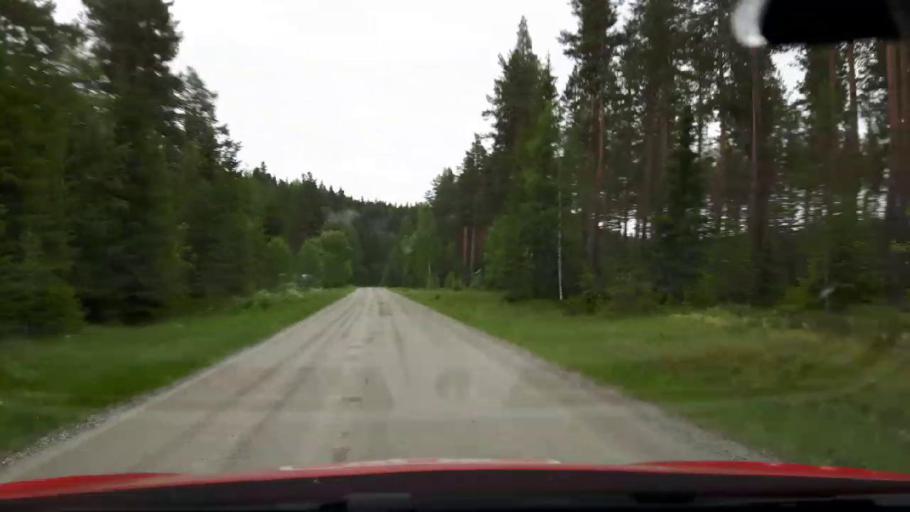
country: SE
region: Jaemtland
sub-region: Ragunda Kommun
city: Hammarstrand
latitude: 63.1997
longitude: 16.1268
